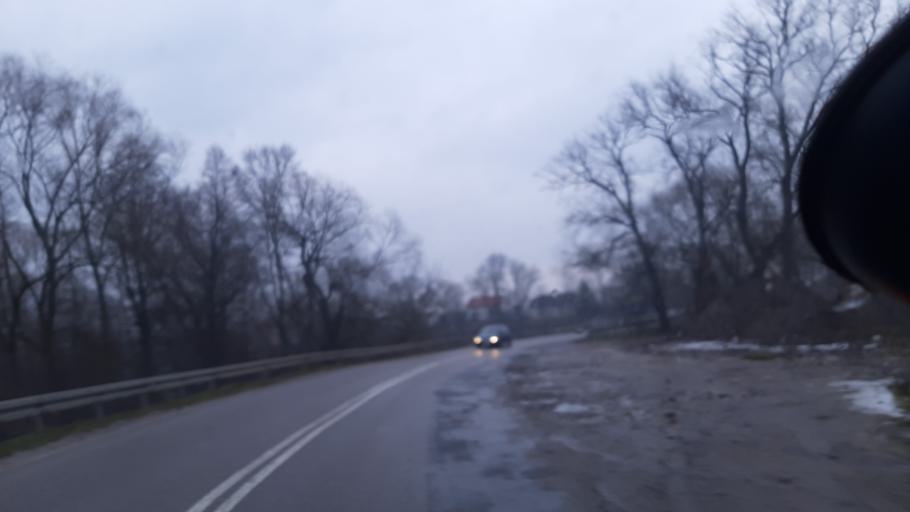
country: PL
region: Lublin Voivodeship
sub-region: Powiat lubartowski
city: Serniki
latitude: 51.4353
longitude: 22.6544
